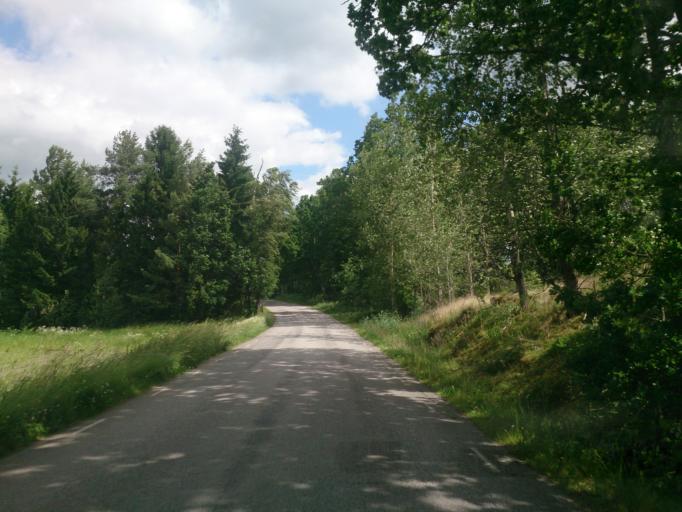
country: SE
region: OEstergoetland
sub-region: Norrkopings Kommun
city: Krokek
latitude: 58.4991
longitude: 16.5751
